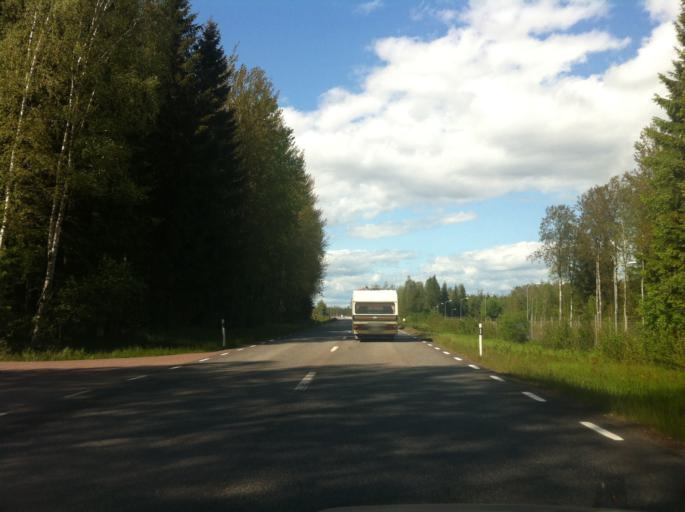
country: SE
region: Vaermland
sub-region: Kristinehamns Kommun
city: Bjorneborg
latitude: 59.1586
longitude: 14.1771
